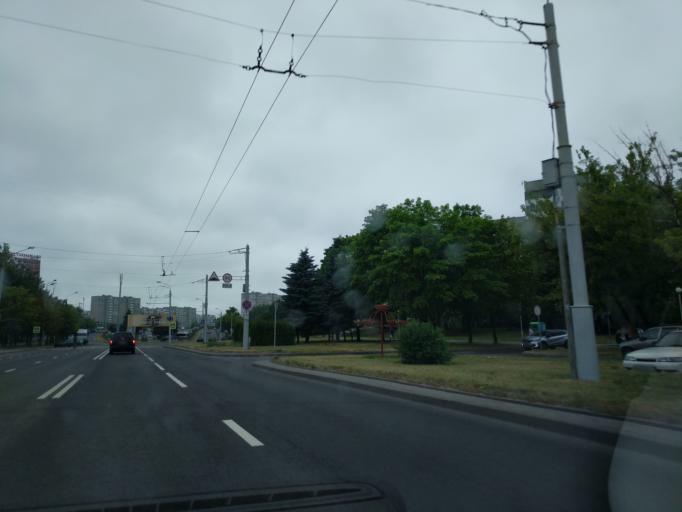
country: BY
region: Minsk
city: Novoye Medvezhino
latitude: 53.8635
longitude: 27.4671
